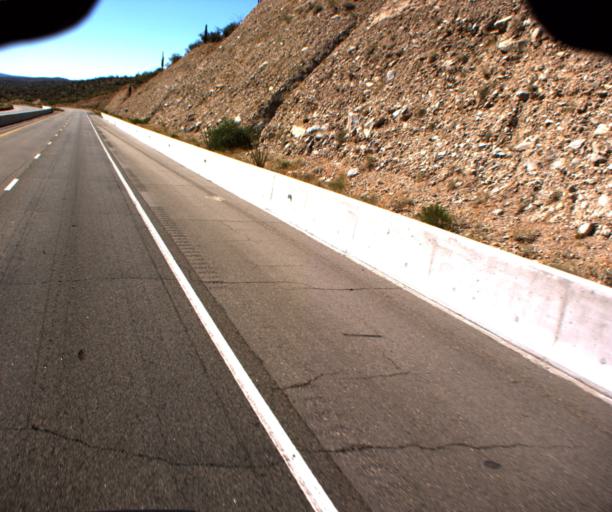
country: US
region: Arizona
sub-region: Yavapai County
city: Bagdad
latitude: 34.4023
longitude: -113.2202
